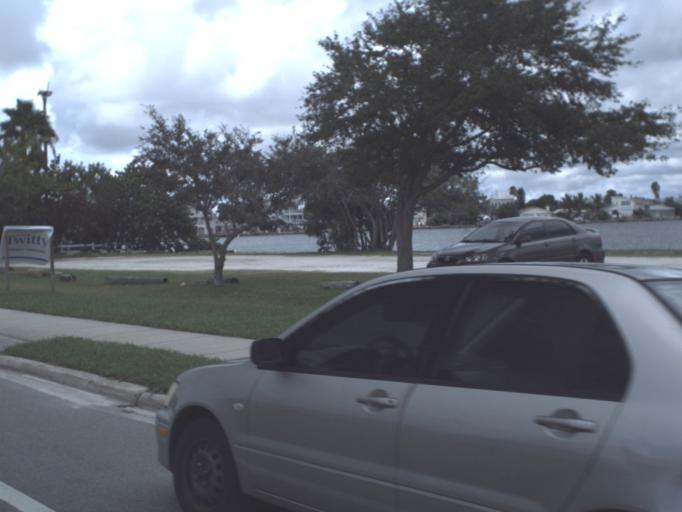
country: US
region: Florida
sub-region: Pinellas County
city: Redington Shores
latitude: 27.8298
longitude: -82.8309
